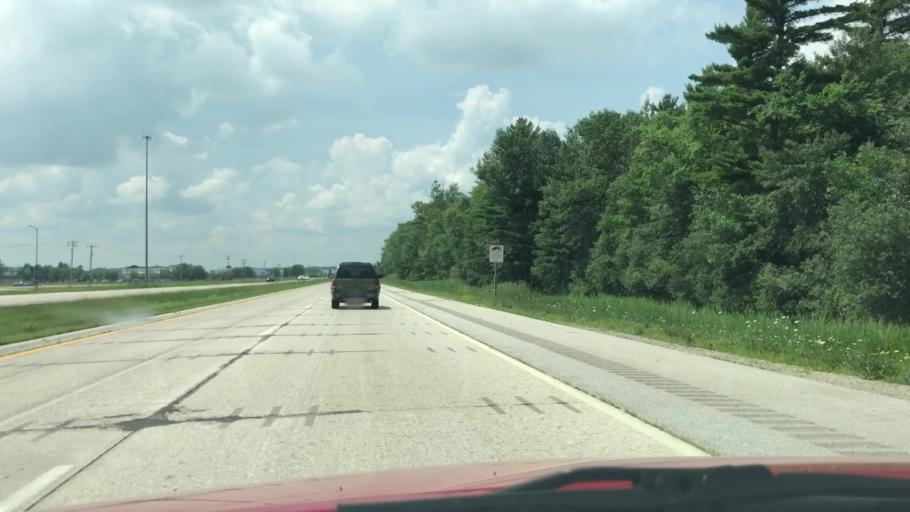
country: US
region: Wisconsin
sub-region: Brown County
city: Ashwaubenon
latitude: 44.4966
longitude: -88.1152
